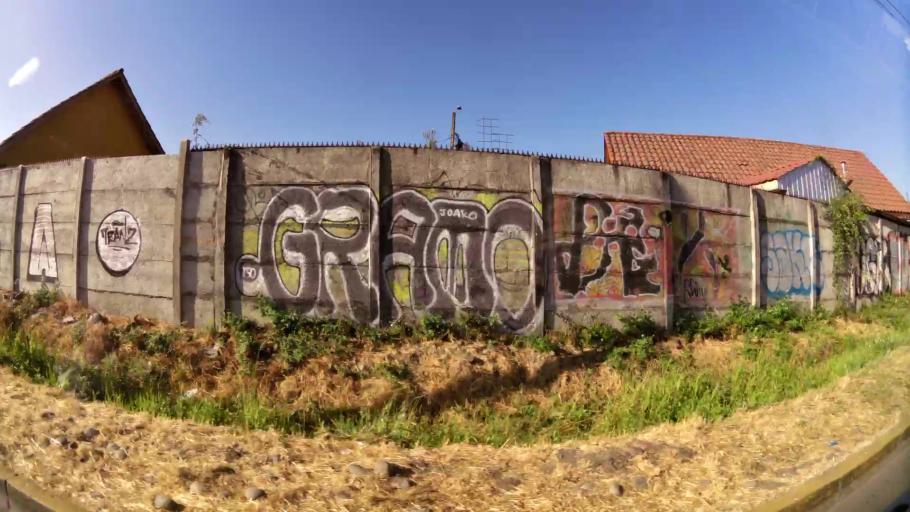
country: CL
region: Maule
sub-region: Provincia de Talca
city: Talca
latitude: -35.4423
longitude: -71.6889
